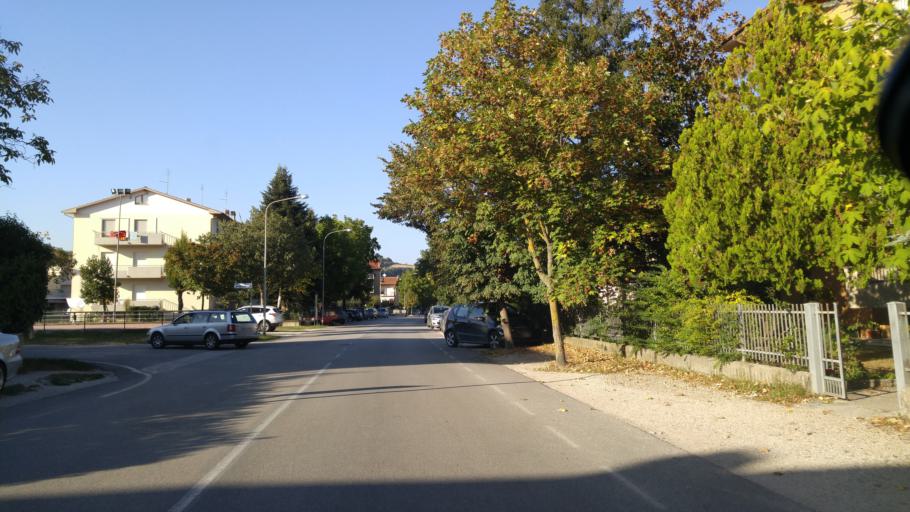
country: IT
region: The Marches
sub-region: Provincia di Pesaro e Urbino
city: Fermignano
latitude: 43.6838
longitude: 12.6475
